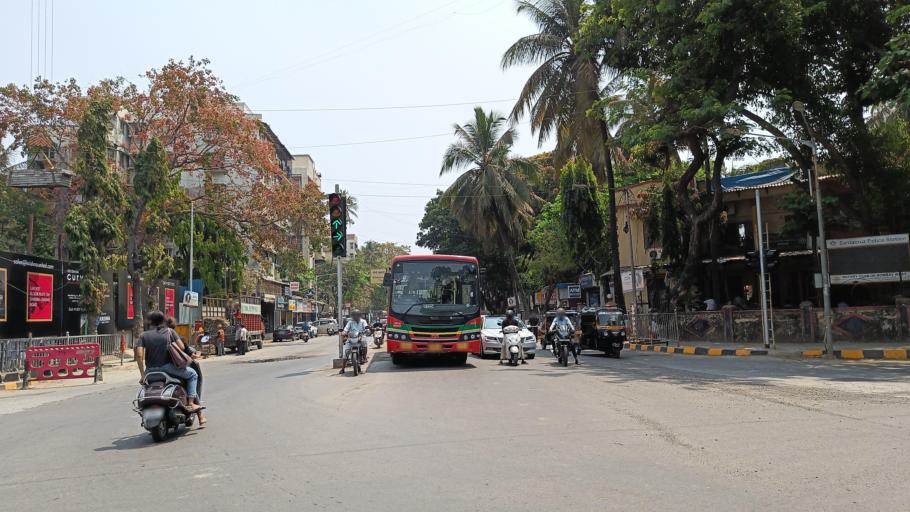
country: IN
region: Maharashtra
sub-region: Mumbai Suburban
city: Mumbai
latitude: 19.0846
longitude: 72.8344
